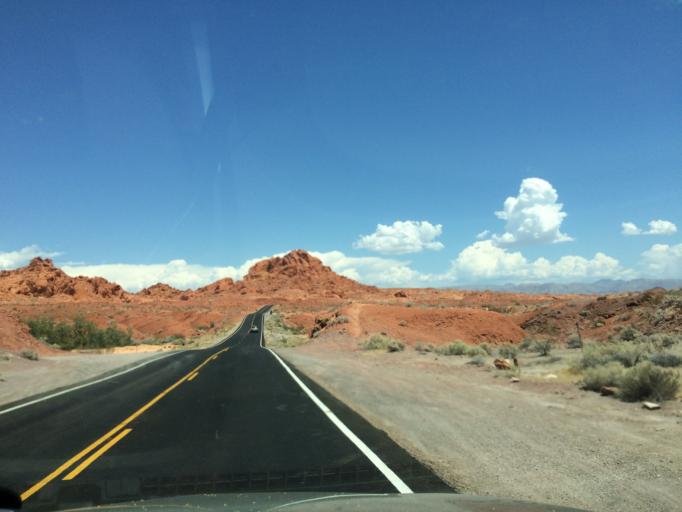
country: US
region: Nevada
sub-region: Clark County
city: Moapa Valley
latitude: 36.4261
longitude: -114.4711
